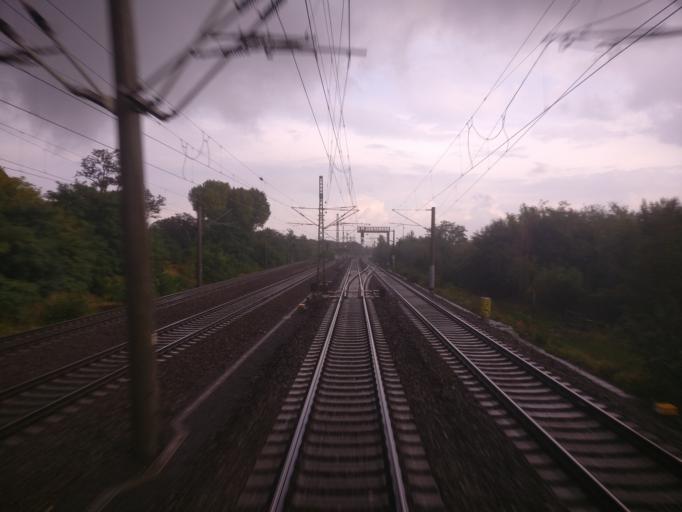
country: DE
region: Saxony
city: Dresden
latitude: 51.0226
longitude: 13.7864
